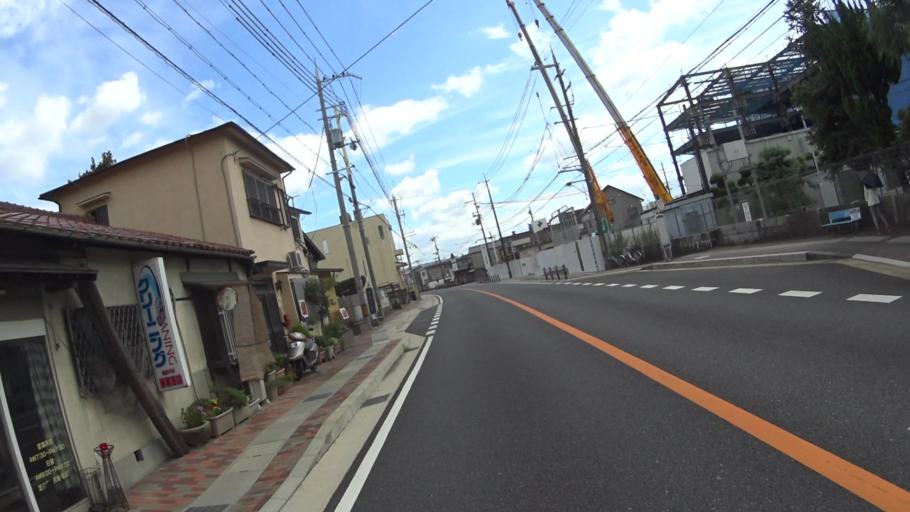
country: JP
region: Kyoto
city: Yawata
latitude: 34.8887
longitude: 135.7217
